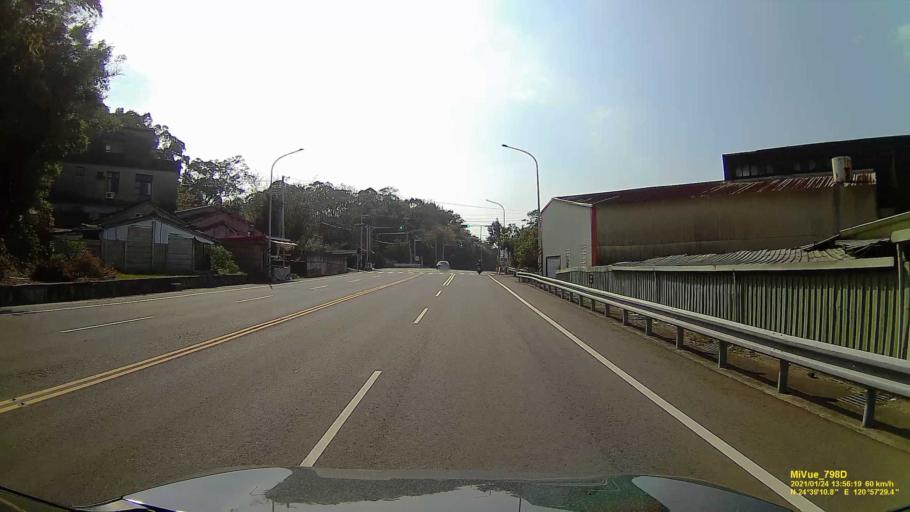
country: TW
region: Taiwan
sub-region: Hsinchu
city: Hsinchu
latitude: 24.6528
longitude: 120.9578
